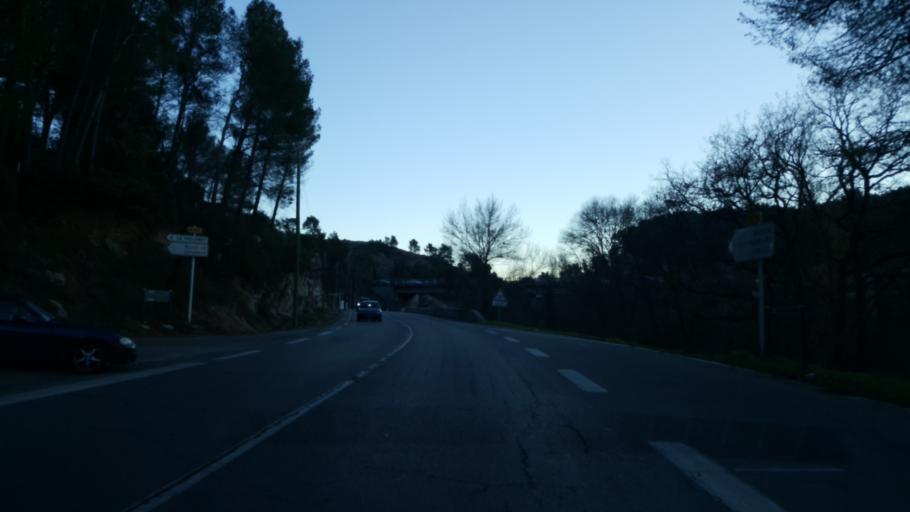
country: FR
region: Provence-Alpes-Cote d'Azur
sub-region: Departement des Bouches-du-Rhone
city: Le Tholonet
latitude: 43.5078
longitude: 5.5072
